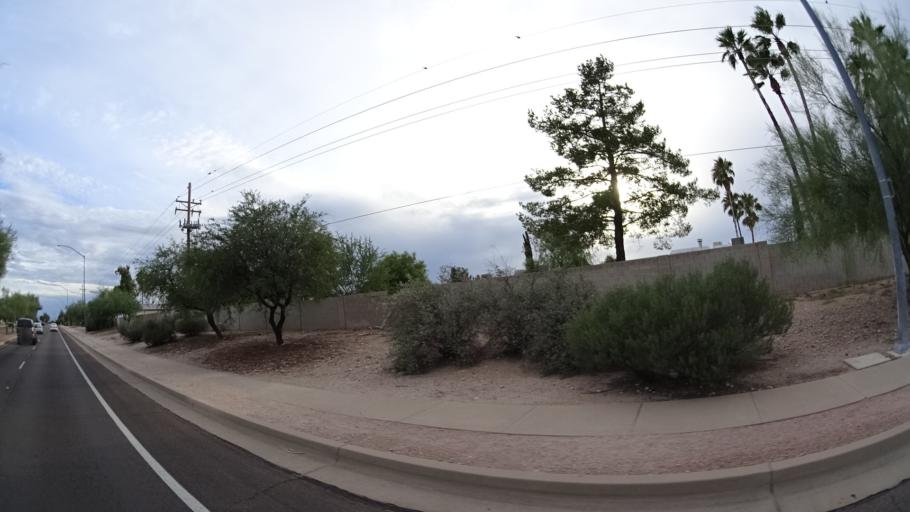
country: US
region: Arizona
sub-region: Pima County
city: South Tucson
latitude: 32.1542
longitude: -110.9351
